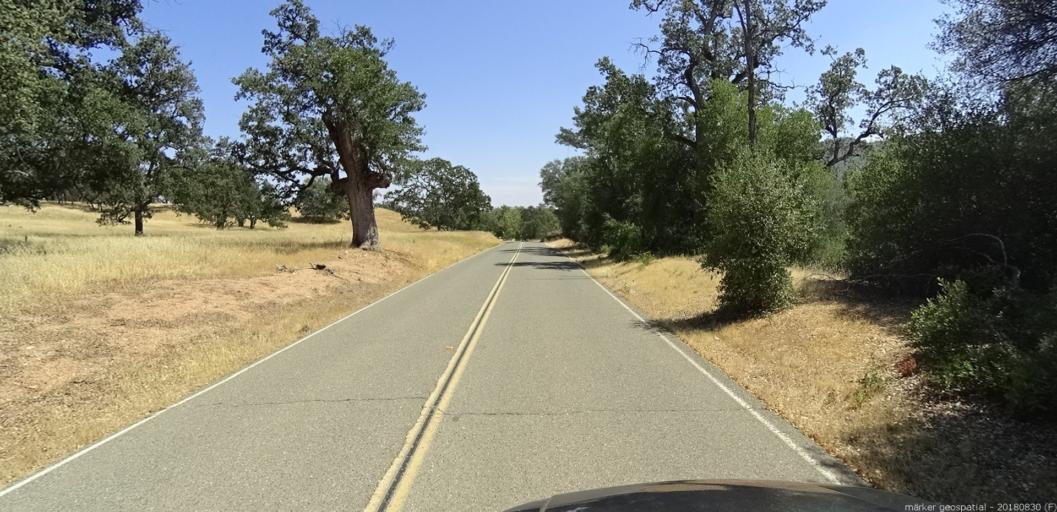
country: US
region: California
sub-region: Monterey County
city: King City
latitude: 35.9769
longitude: -121.3442
